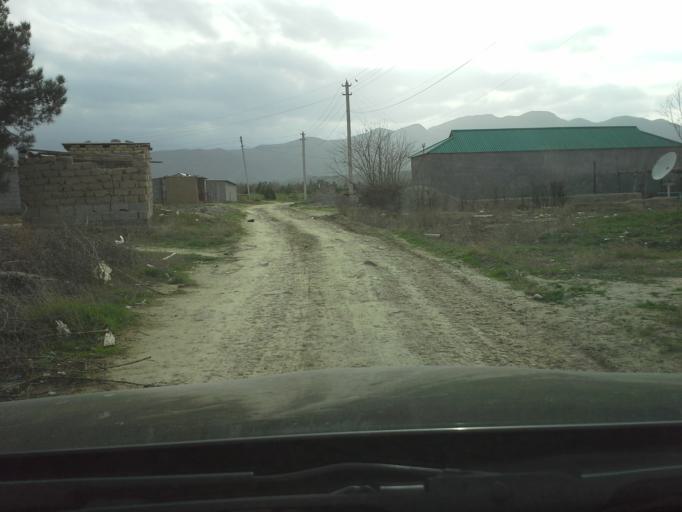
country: TM
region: Ahal
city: Abadan
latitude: 37.9593
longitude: 58.2305
